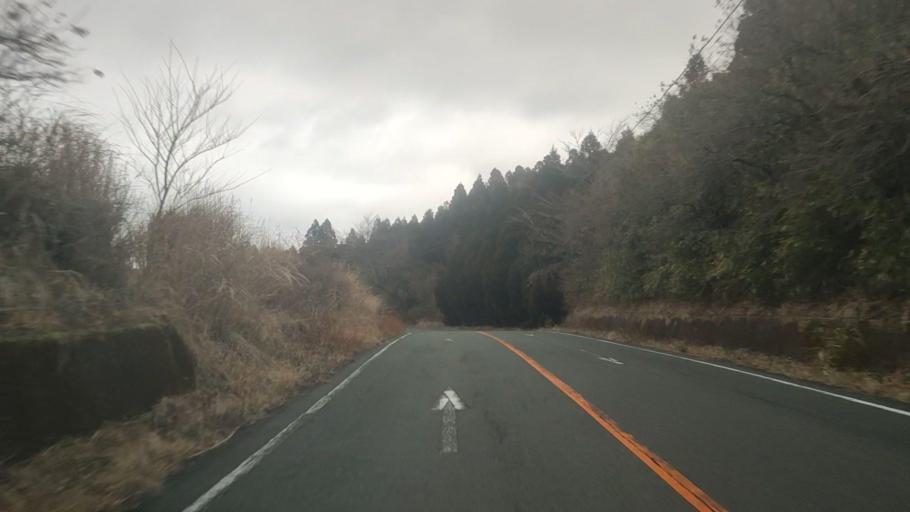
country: JP
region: Kumamoto
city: Aso
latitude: 32.8832
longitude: 131.1710
